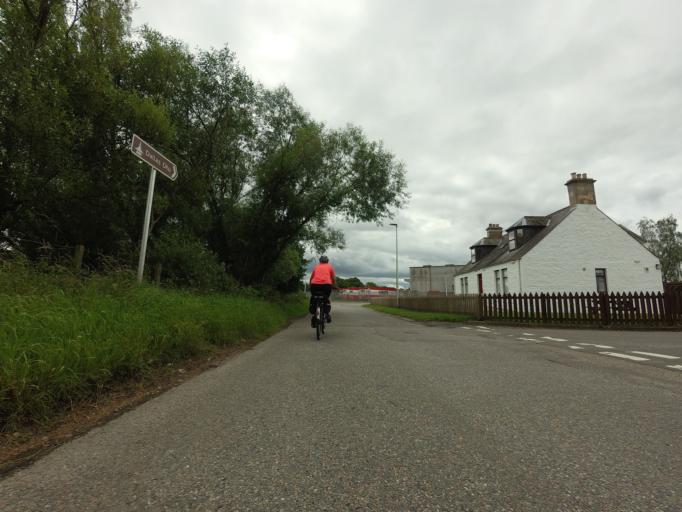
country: GB
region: Scotland
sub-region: Moray
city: Forres
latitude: 57.6132
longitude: -3.6195
